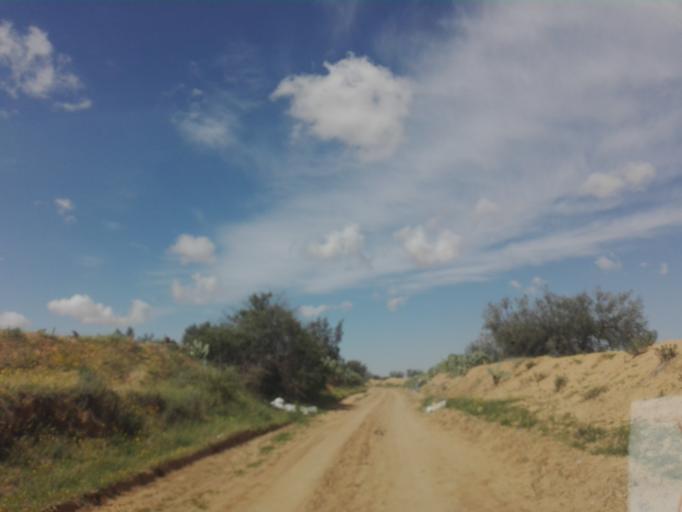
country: TN
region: Safaqis
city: Sfax
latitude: 34.7347
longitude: 10.5166
